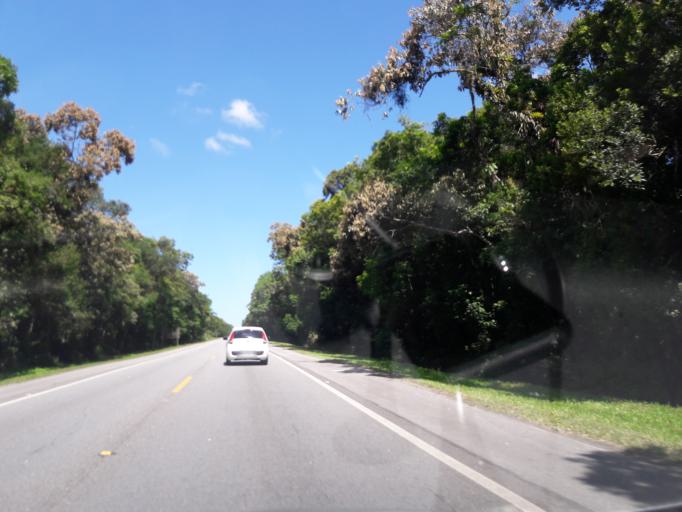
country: BR
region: Parana
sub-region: Pontal Do Parana
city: Pontal do Parana
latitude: -25.6021
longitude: -48.5571
